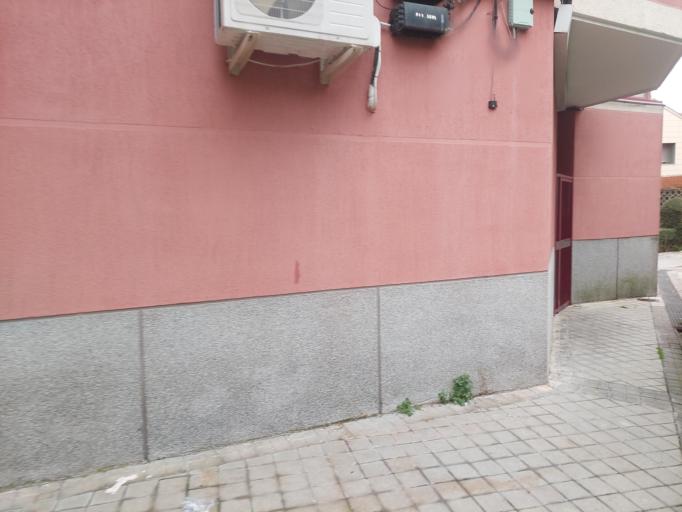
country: ES
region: Madrid
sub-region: Provincia de Madrid
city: Leganes
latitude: 40.3274
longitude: -3.7692
